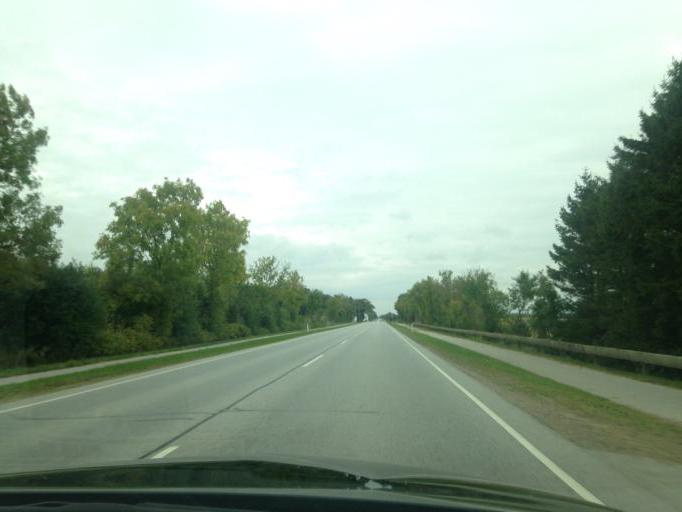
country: DK
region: South Denmark
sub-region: Haderslev Kommune
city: Haderslev
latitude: 55.2790
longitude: 9.4980
